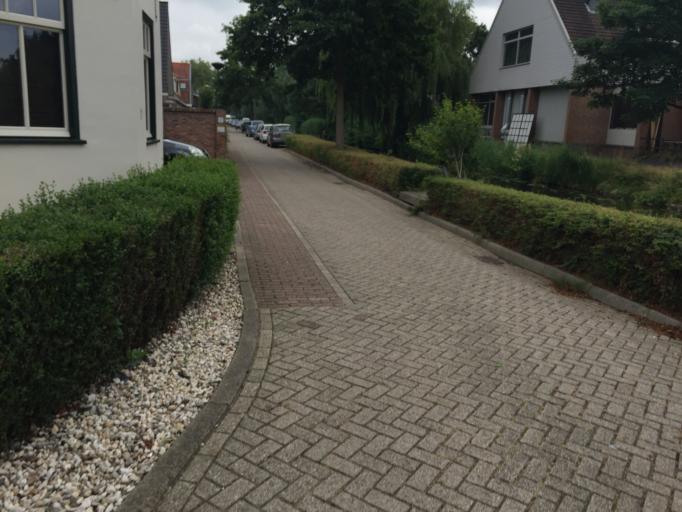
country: NL
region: Utrecht
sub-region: Gemeente Woerden
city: Woerden
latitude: 52.0839
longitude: 4.8925
